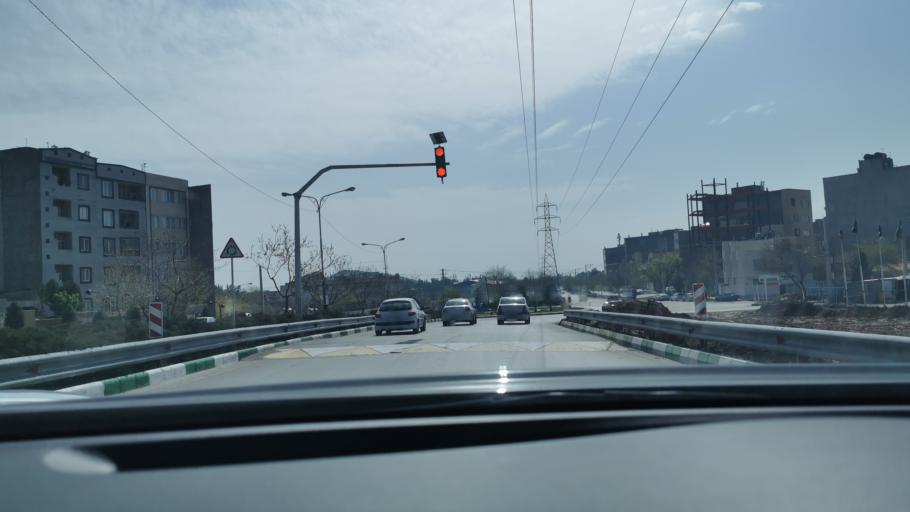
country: IR
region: Razavi Khorasan
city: Mashhad
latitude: 36.2836
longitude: 59.5430
